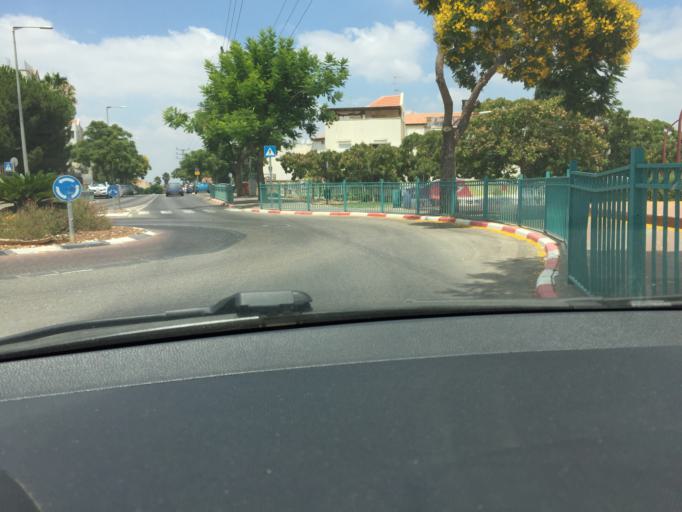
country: IL
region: Jerusalem
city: Ariel
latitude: 32.1078
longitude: 35.1897
